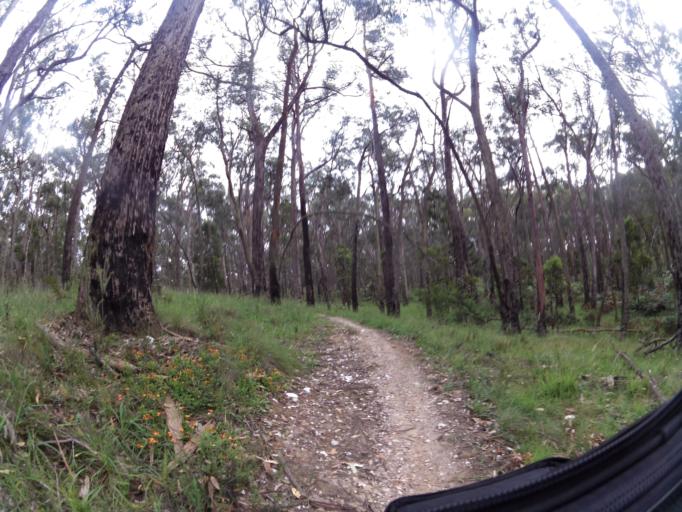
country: AU
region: Victoria
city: Brown Hill
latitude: -37.5251
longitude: 143.9059
